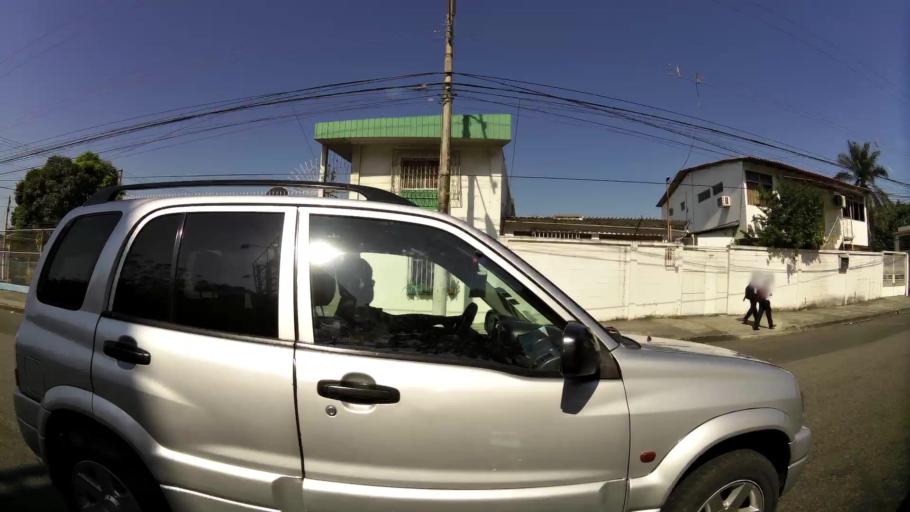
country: EC
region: Guayas
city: Guayaquil
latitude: -2.1639
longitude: -79.9215
